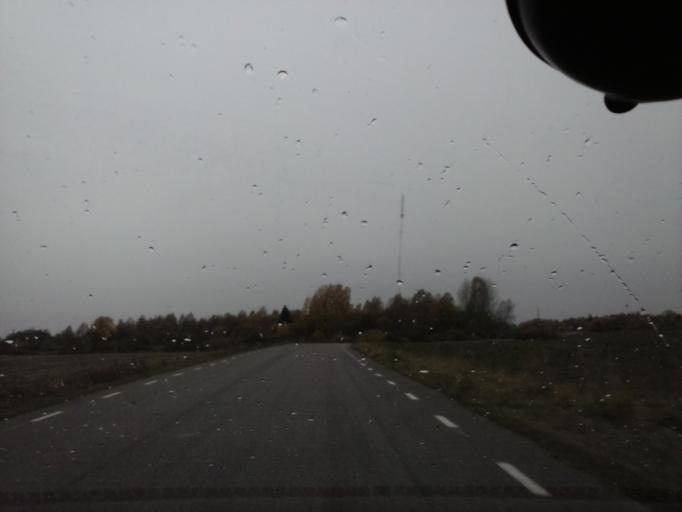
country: EE
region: Viljandimaa
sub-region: Vohma linn
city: Vohma
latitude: 58.6878
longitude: 25.6513
